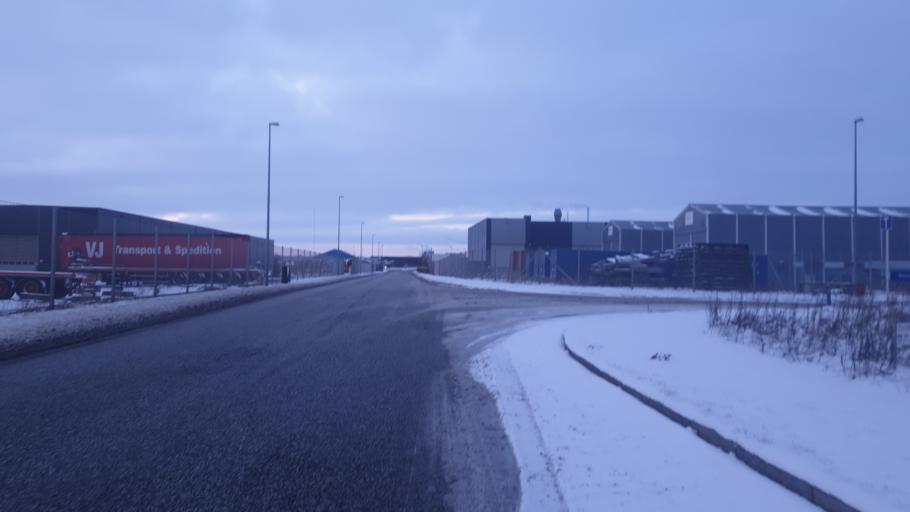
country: DK
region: Central Jutland
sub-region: Hedensted Kommune
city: Hedensted
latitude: 55.7899
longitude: 9.6792
